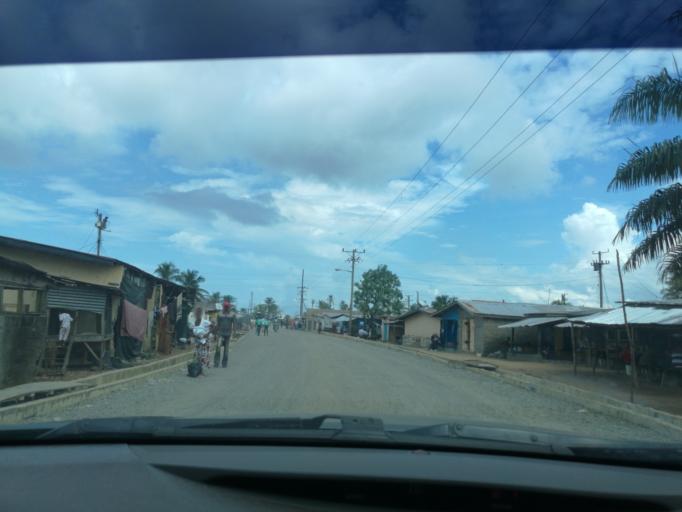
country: LR
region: Montserrado
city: Monrovia
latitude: 6.3349
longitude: -10.7849
